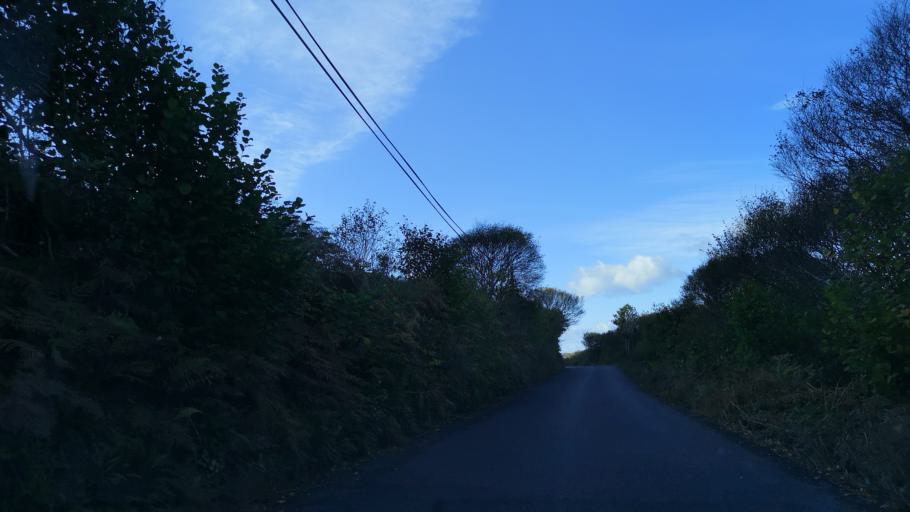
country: IE
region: Connaught
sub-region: County Galway
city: Clifden
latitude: 53.5040
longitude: -10.0696
